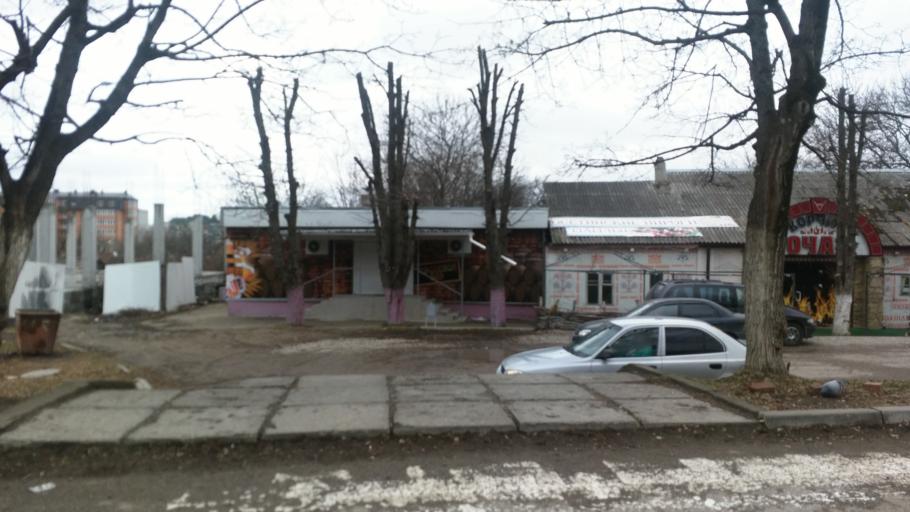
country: RU
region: Stavropol'skiy
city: Zheleznovodsk
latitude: 44.1406
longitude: 43.0126
